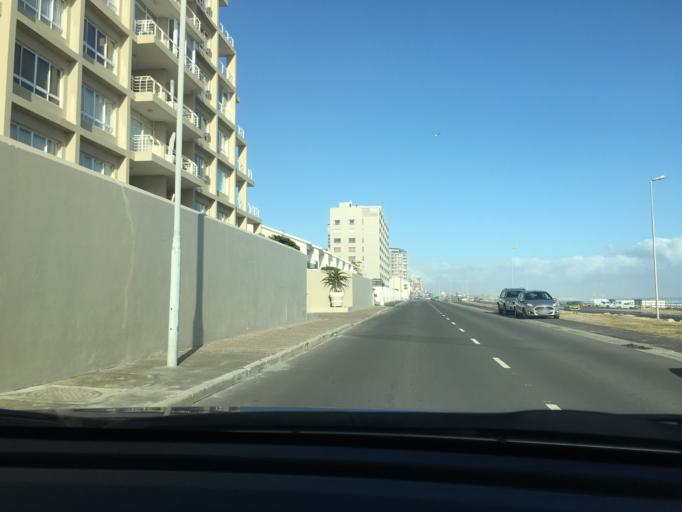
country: ZA
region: Western Cape
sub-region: City of Cape Town
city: Sunset Beach
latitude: -33.8186
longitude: 18.4747
